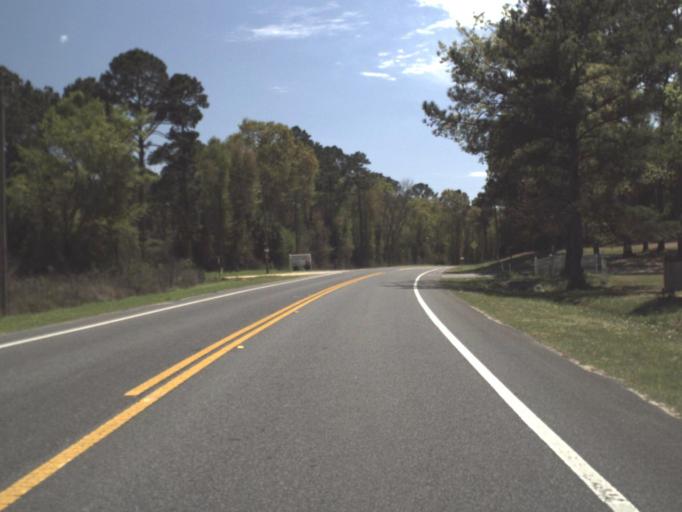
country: US
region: Alabama
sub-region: Geneva County
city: Geneva
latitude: 30.8628
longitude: -85.9441
